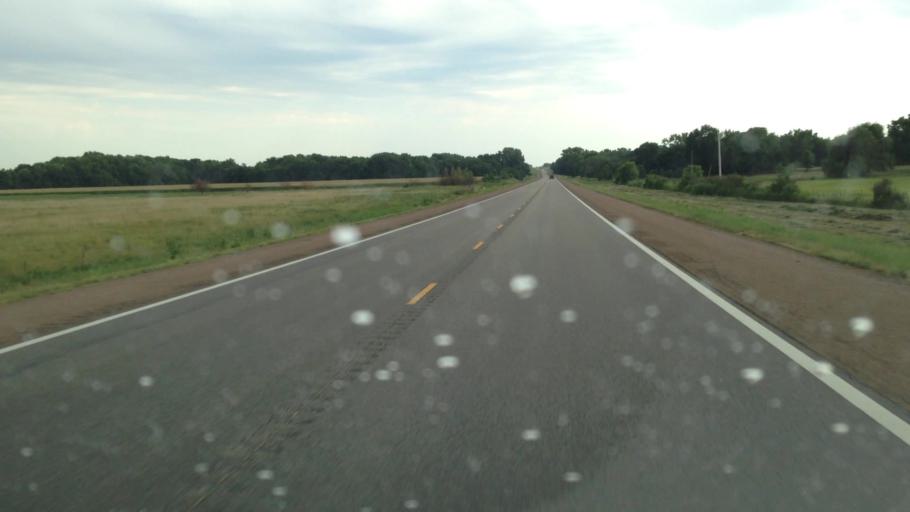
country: US
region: Kansas
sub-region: Woodson County
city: Yates Center
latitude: 38.0351
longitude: -95.7390
